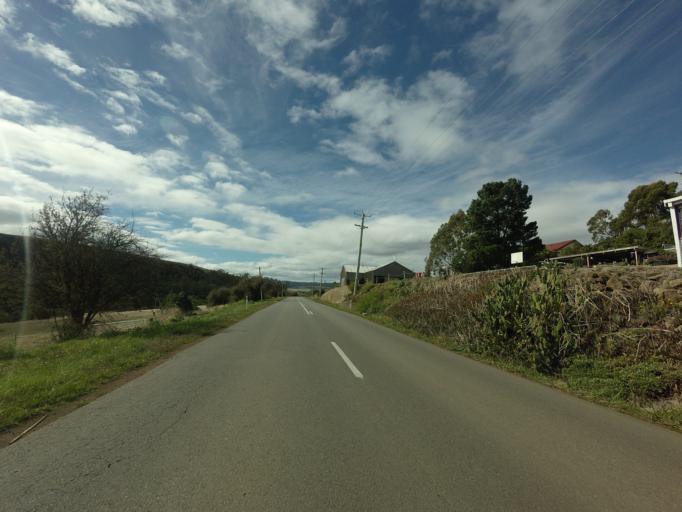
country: AU
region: Tasmania
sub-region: Derwent Valley
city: New Norfolk
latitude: -42.6994
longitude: 146.9190
